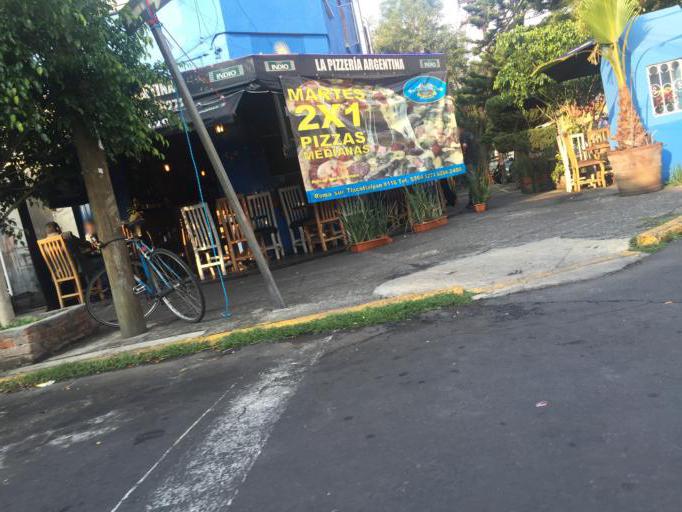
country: MX
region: Mexico City
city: Benito Juarez
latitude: 19.4034
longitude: -99.1657
